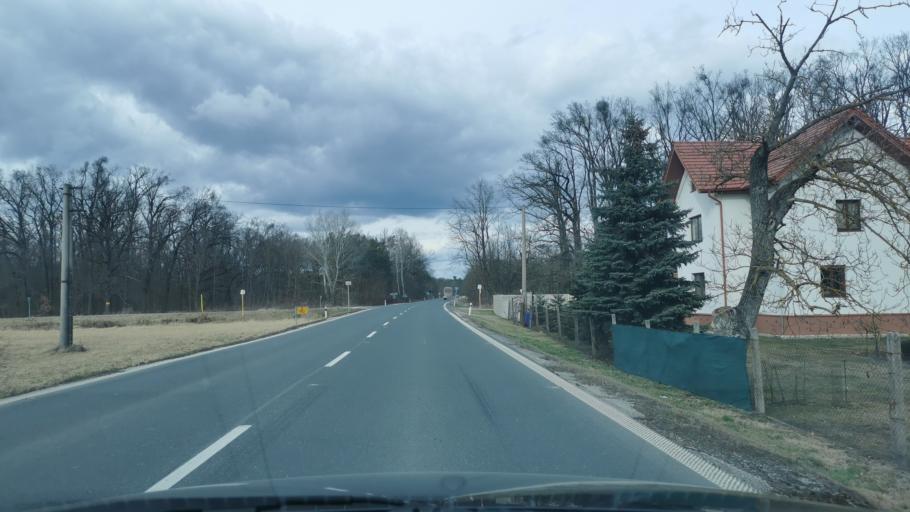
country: CZ
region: South Moravian
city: Tvrdonice
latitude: 48.6992
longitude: 17.0401
